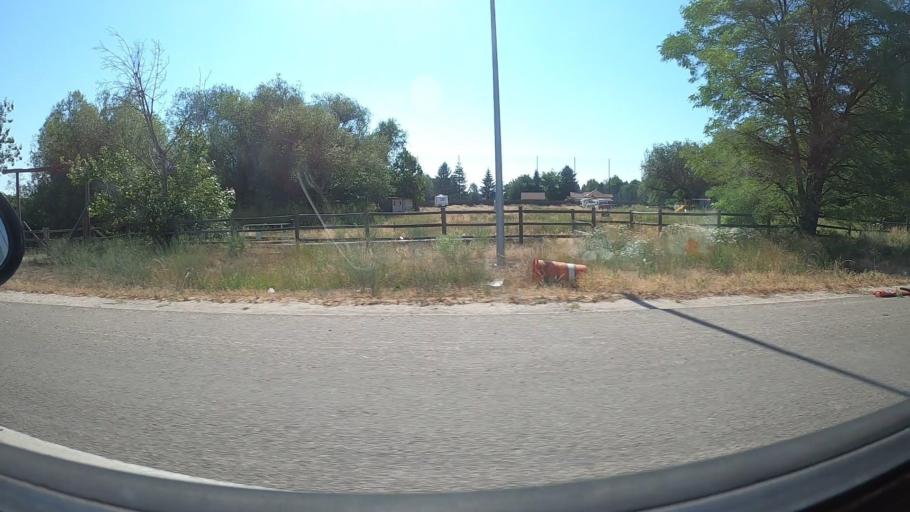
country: US
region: Idaho
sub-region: Ada County
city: Eagle
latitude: 43.6709
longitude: -116.3545
